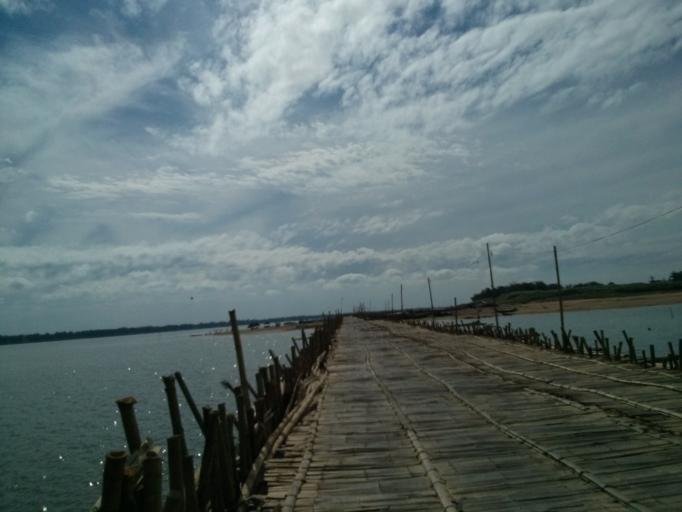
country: KH
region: Kampong Cham
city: Kampong Cham
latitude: 11.9739
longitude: 105.4624
